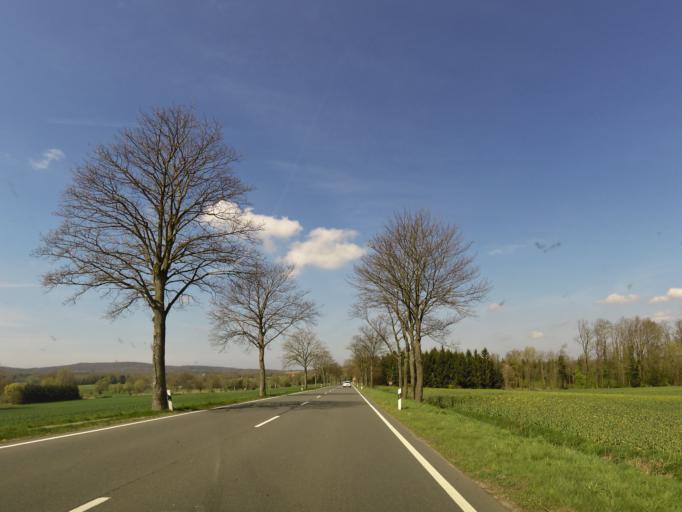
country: DE
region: Lower Saxony
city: Wolpinghausen
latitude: 52.4335
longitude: 9.2652
